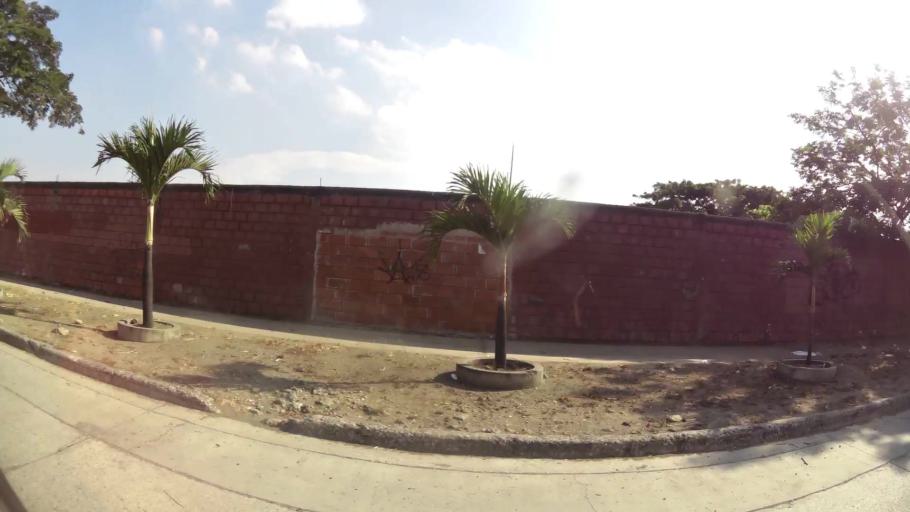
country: EC
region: Guayas
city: Guayaquil
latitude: -2.1333
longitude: -79.9298
